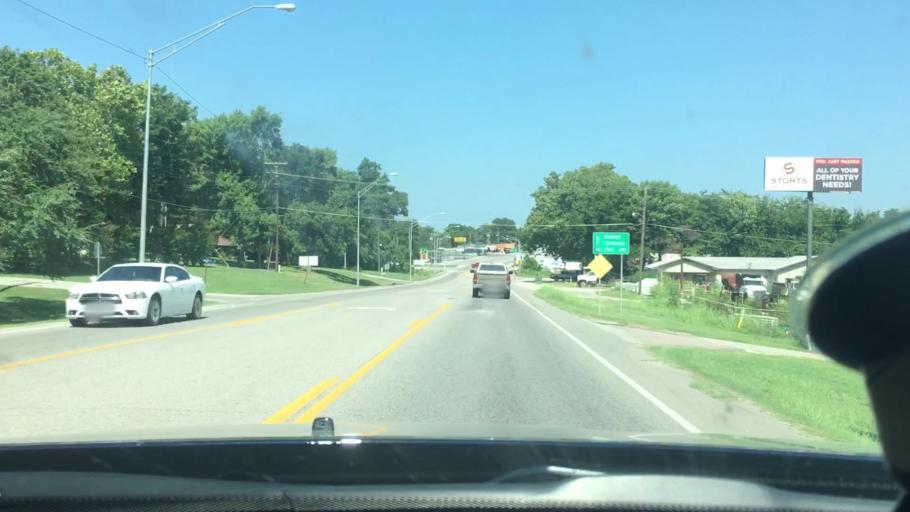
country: US
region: Oklahoma
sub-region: Marshall County
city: Madill
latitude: 34.0818
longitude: -96.7663
